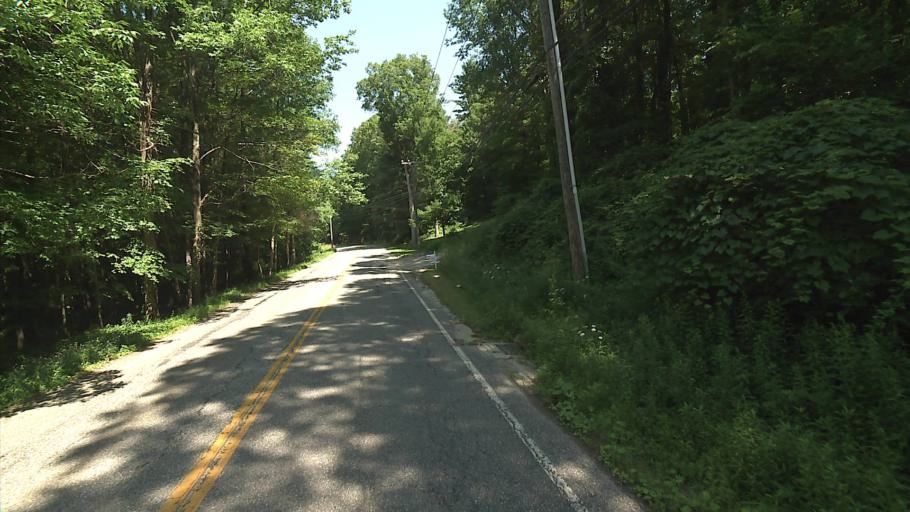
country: US
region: Connecticut
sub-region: Litchfield County
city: Canaan
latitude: 41.8574
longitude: -73.3291
